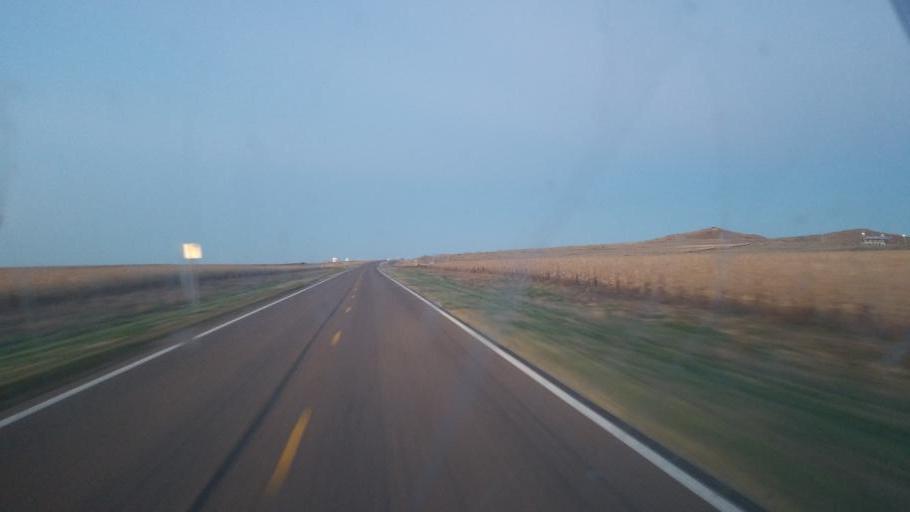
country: US
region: Kansas
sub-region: Wallace County
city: Sharon Springs
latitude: 39.0099
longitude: -101.3656
